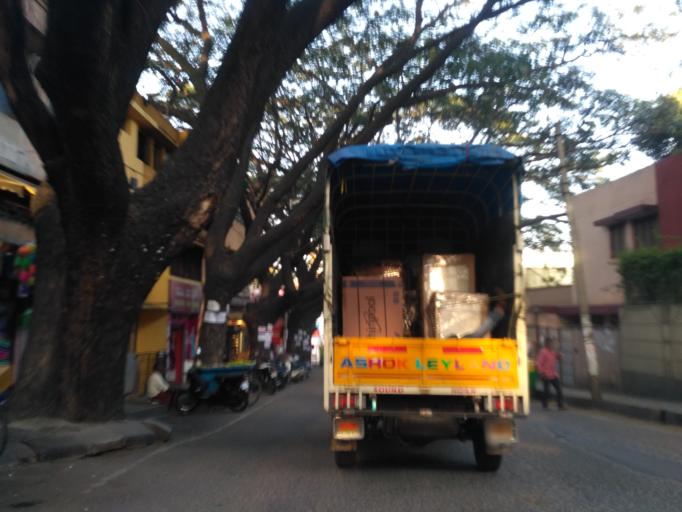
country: IN
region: Karnataka
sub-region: Bangalore Urban
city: Bangalore
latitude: 12.9583
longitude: 77.5351
